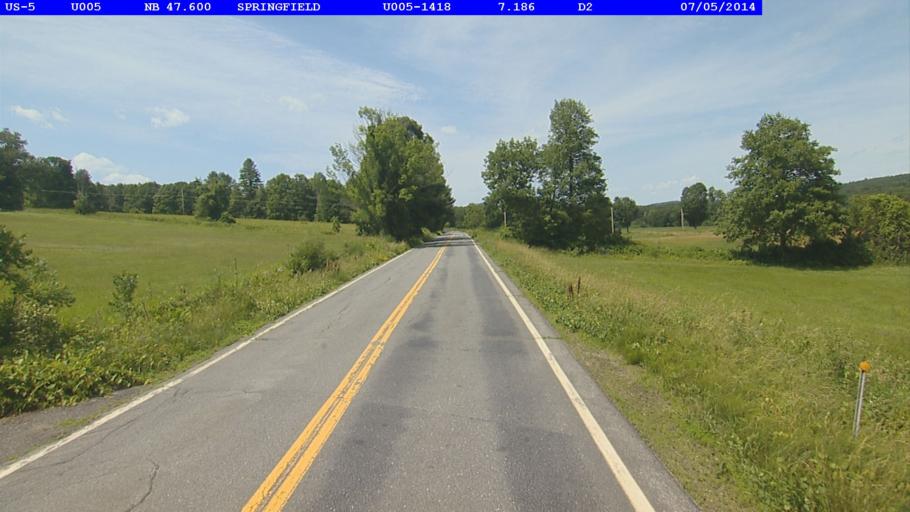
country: US
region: New Hampshire
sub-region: Sullivan County
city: Charlestown
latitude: 43.3139
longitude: -72.3997
